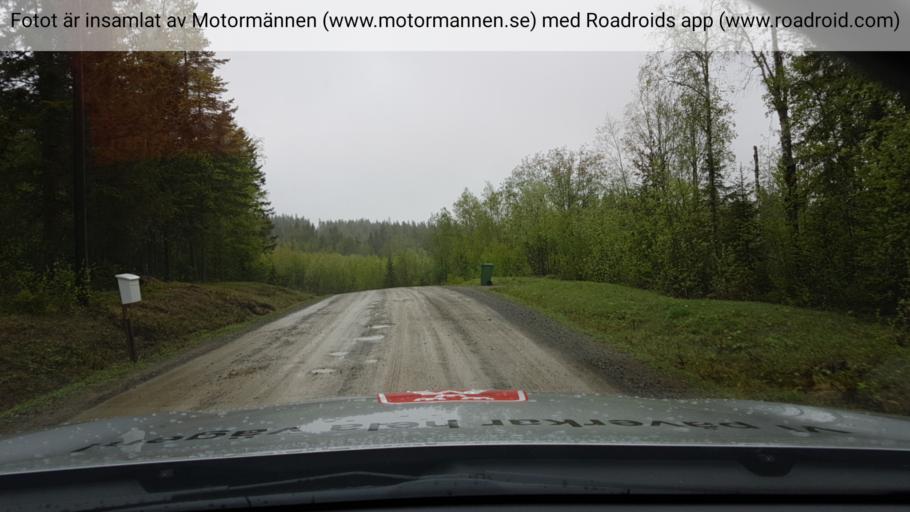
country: SE
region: Jaemtland
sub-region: Bergs Kommun
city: Hoverberg
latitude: 62.9826
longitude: 14.2027
